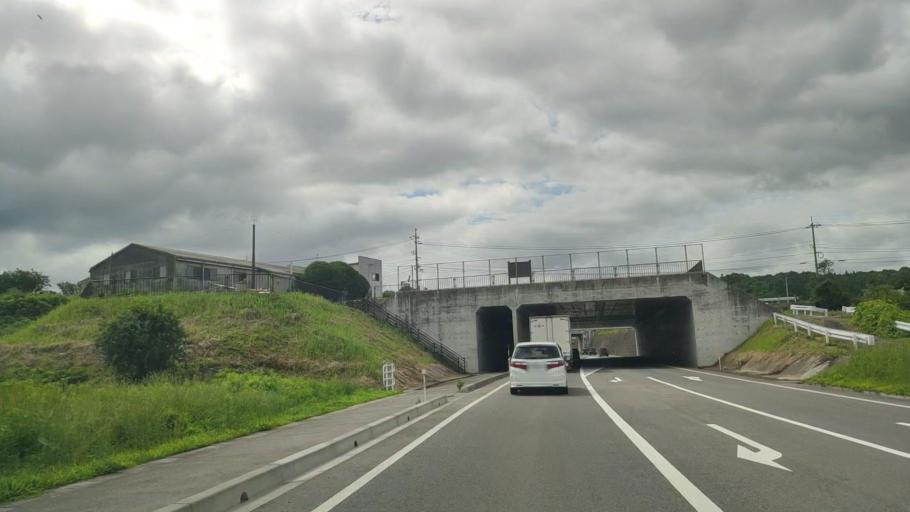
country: JP
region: Tottori
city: Yonago
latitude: 35.3831
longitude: 133.3872
